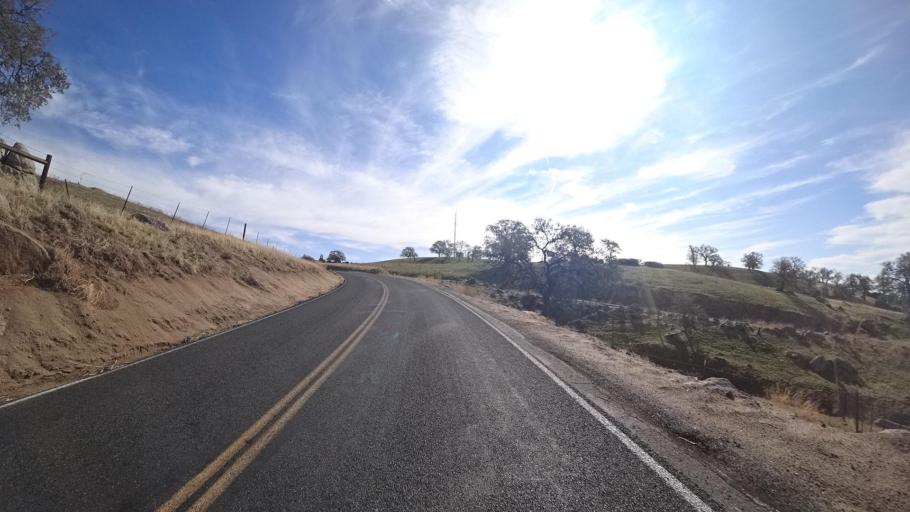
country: US
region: California
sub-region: Kern County
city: Oildale
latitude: 35.6185
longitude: -118.8536
